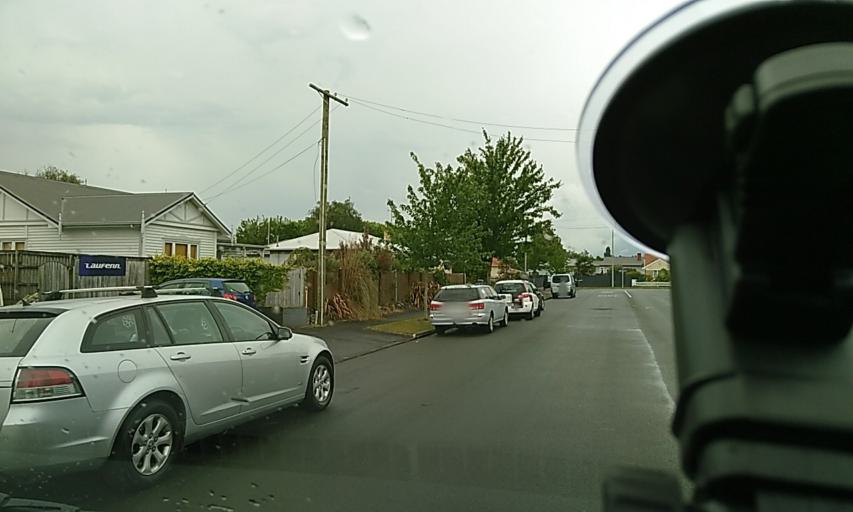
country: NZ
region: Waikato
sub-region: Hamilton City
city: Hamilton
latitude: -37.7849
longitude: 175.2627
